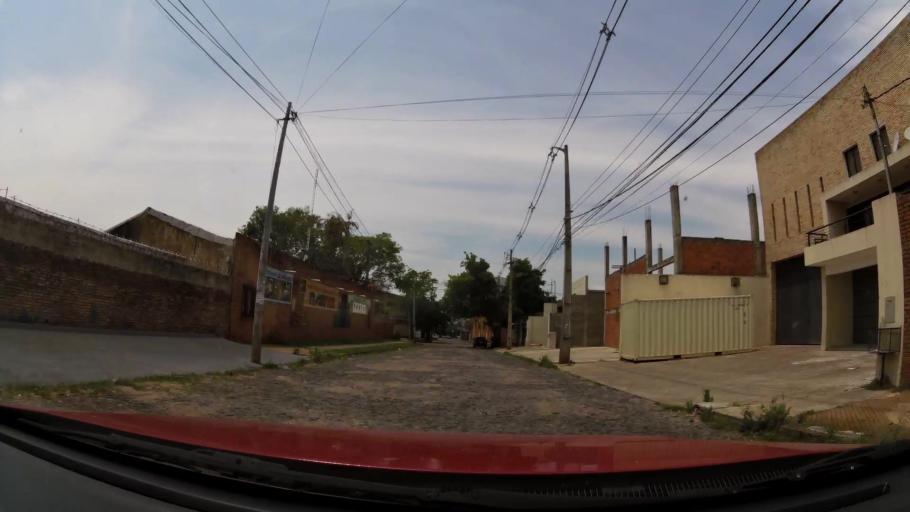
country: PY
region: Central
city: Lambare
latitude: -25.3161
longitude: -57.5679
